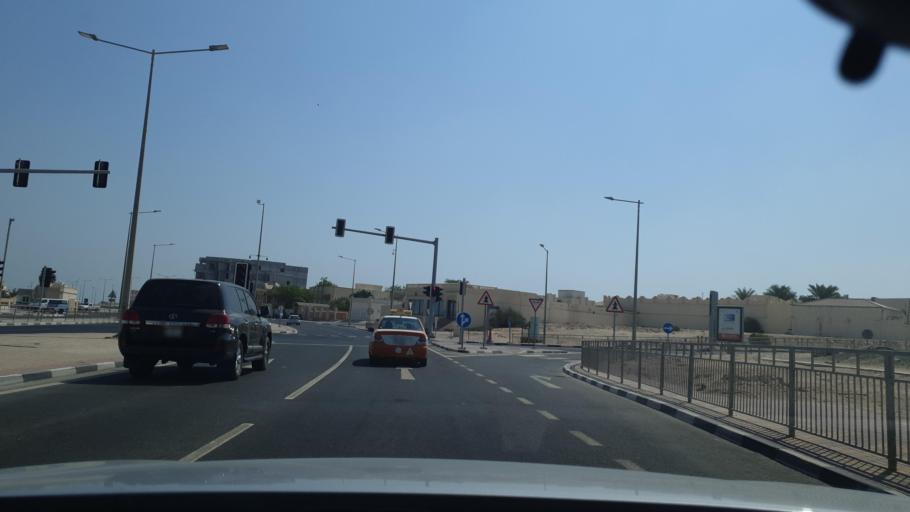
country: QA
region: Al Khawr
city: Al Khawr
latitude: 25.6865
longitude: 51.5086
